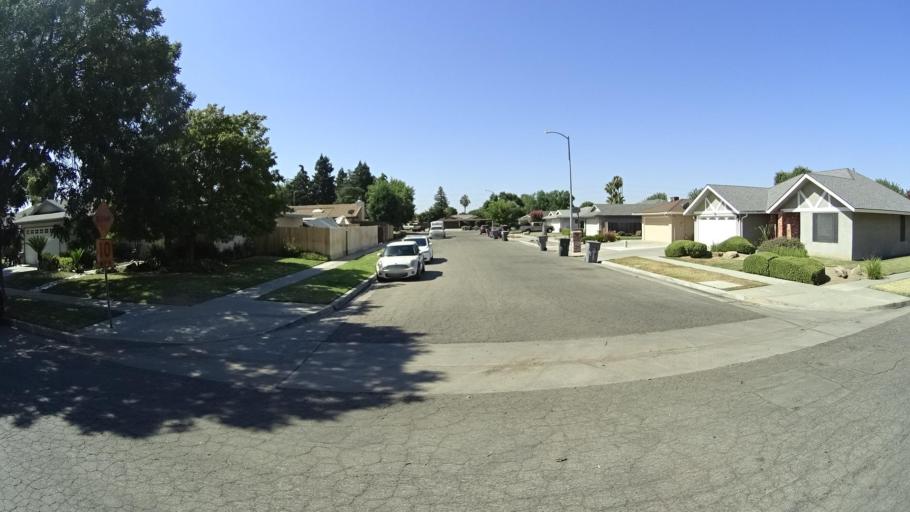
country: US
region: California
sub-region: Fresno County
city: Sunnyside
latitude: 36.7474
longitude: -119.6857
